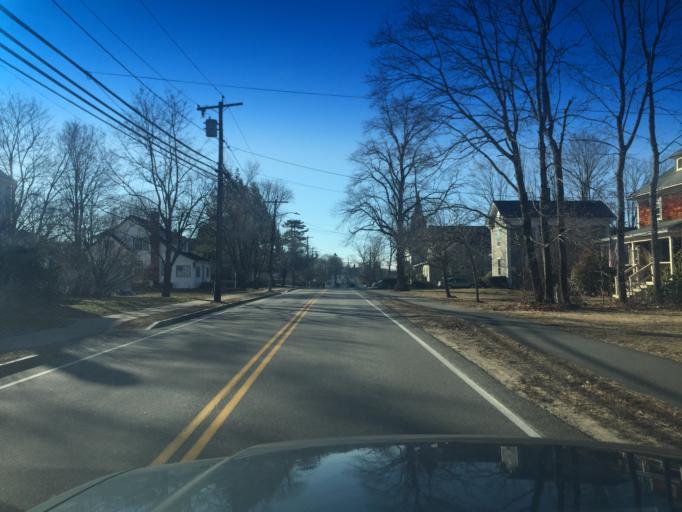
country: US
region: Massachusetts
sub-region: Norfolk County
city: Millis
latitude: 42.1718
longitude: -71.3594
